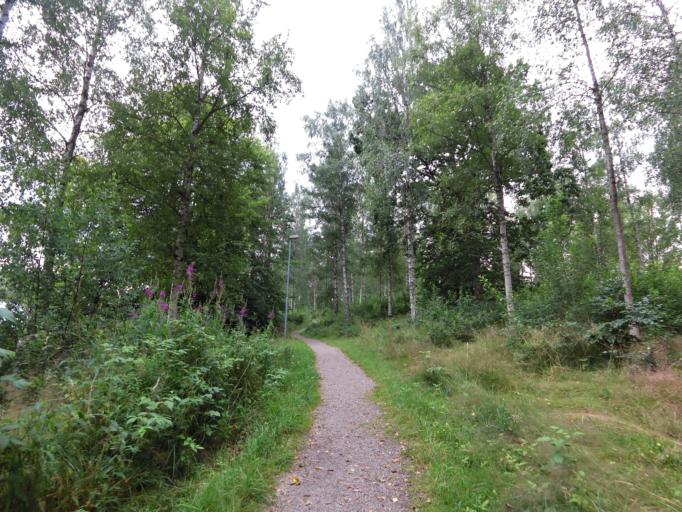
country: SE
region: Blekinge
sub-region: Olofstroms Kommun
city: Olofstroem
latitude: 56.3499
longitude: 14.5924
